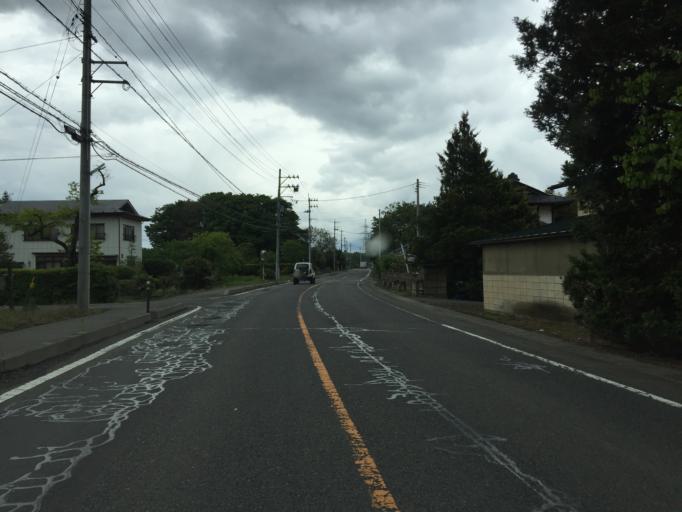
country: JP
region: Fukushima
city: Sukagawa
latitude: 37.1949
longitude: 140.3620
